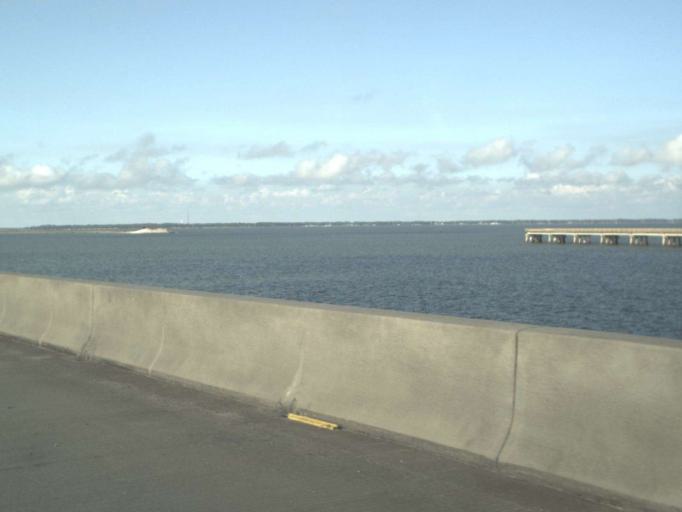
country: US
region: Florida
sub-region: Franklin County
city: Eastpoint
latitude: 29.6773
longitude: -84.8736
